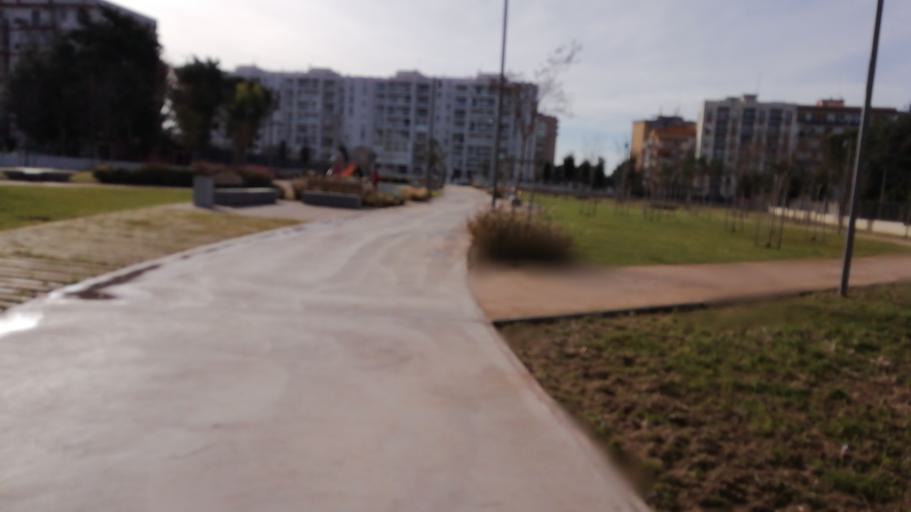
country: IT
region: Apulia
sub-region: Provincia di Bari
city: Triggiano
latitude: 41.1044
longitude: 16.9156
